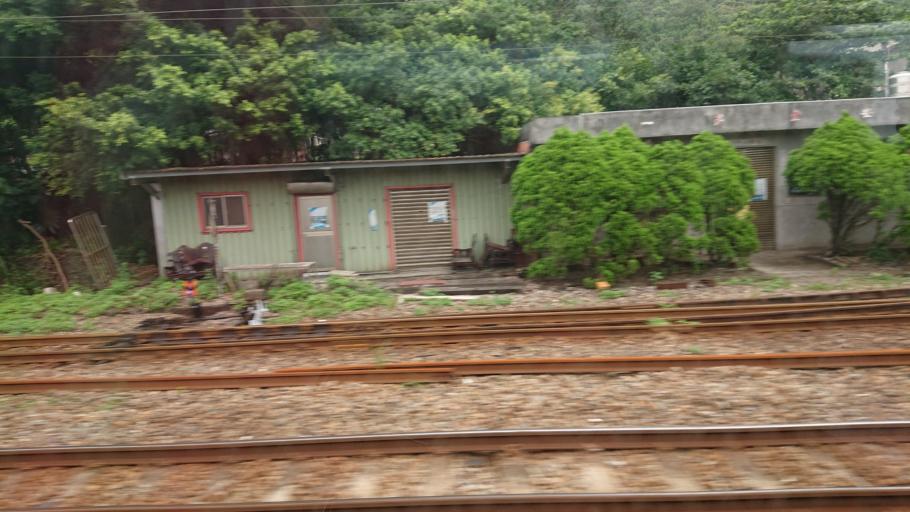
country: TW
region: Taiwan
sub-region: Keelung
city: Keelung
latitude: 24.9672
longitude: 121.9232
